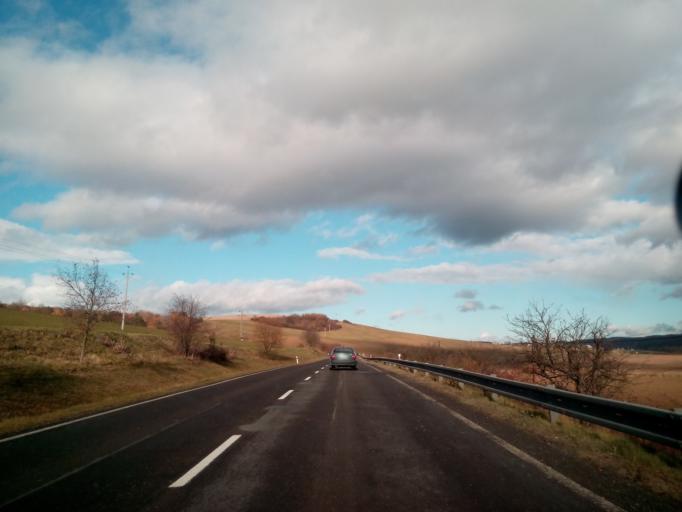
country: SK
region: Presovsky
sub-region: Okres Bardejov
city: Bardejov
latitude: 49.1741
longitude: 21.3071
